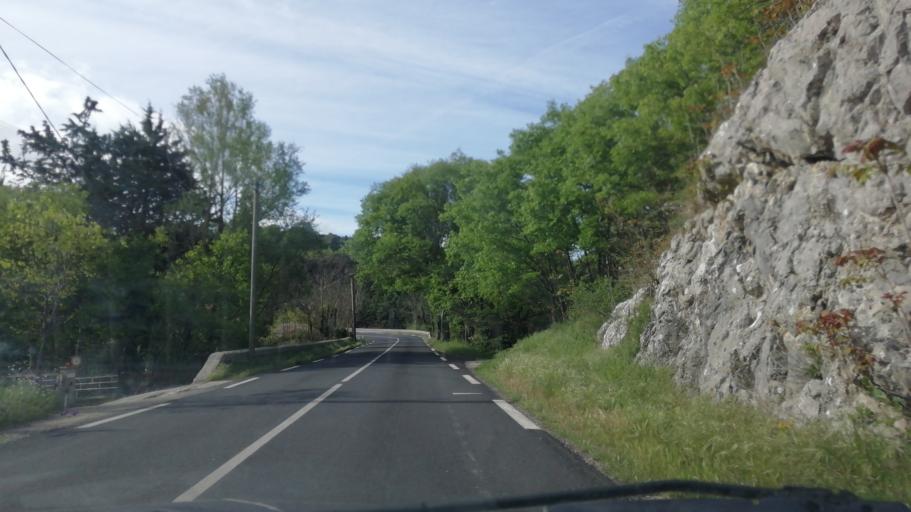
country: FR
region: Languedoc-Roussillon
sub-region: Departement de l'Herault
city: Saint-Martin-de-Londres
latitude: 43.7740
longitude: 3.7206
